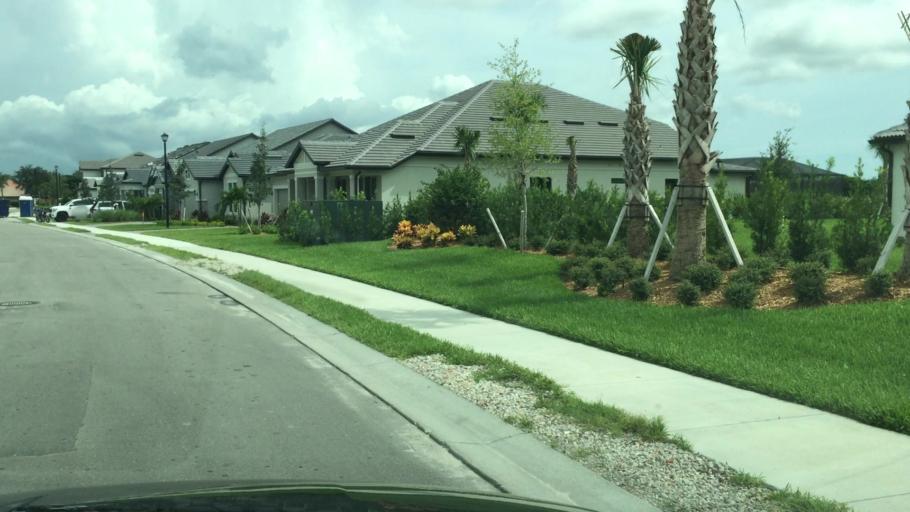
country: US
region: Florida
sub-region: Lee County
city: Three Oaks
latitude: 26.4877
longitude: -81.8031
